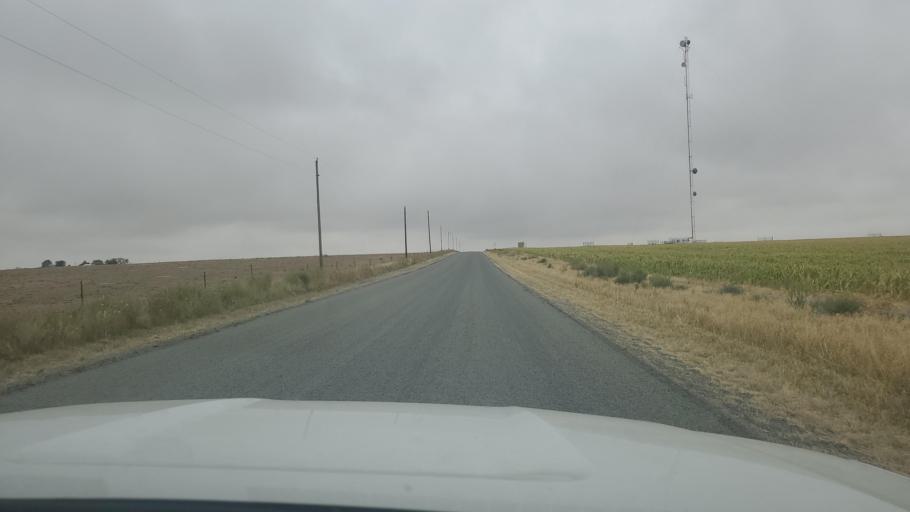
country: US
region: Colorado
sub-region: Weld County
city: Lochbuie
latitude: 39.9200
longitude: -104.6024
